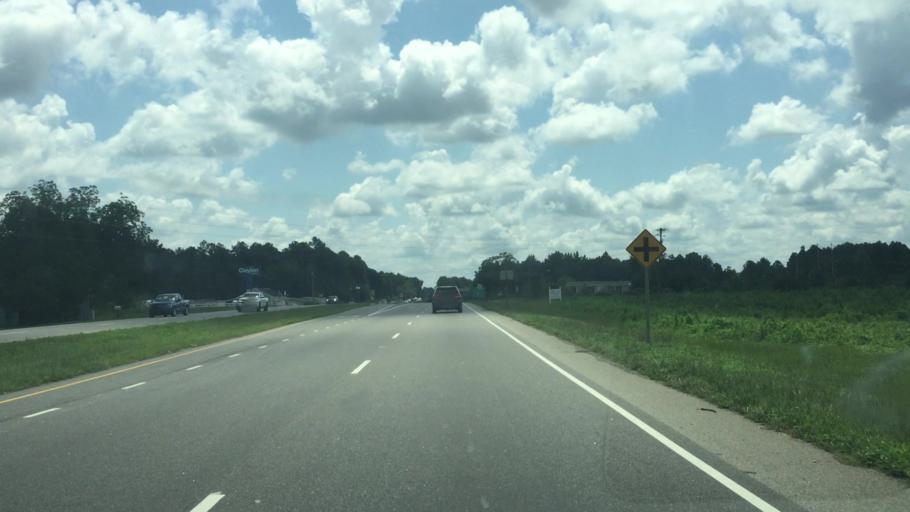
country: US
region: North Carolina
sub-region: Scotland County
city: Laurel Hill
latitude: 34.7938
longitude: -79.5133
